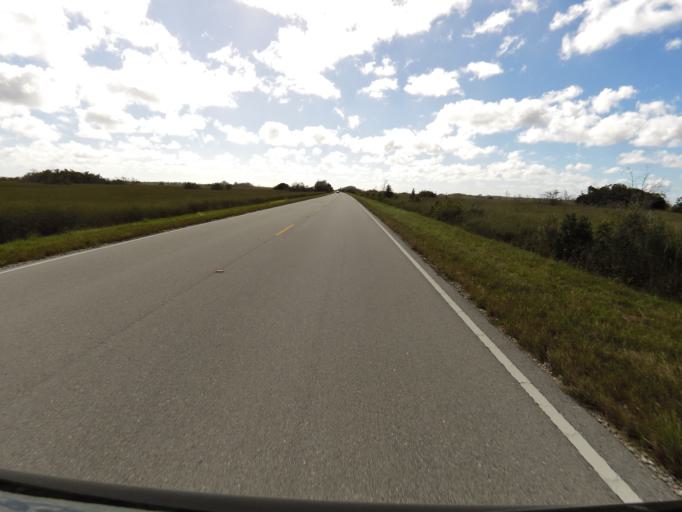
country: US
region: Florida
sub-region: Miami-Dade County
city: Florida City
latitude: 25.3813
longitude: -80.8106
